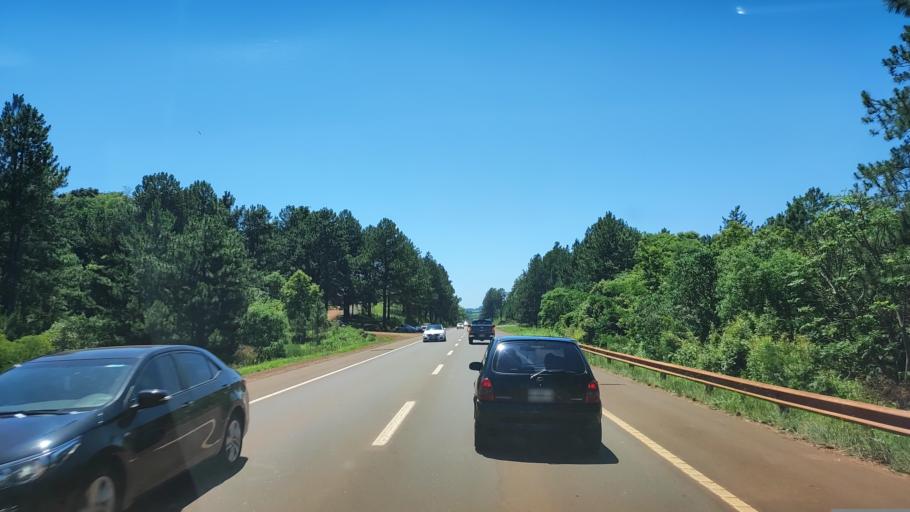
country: AR
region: Misiones
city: Aristobulo del Valle
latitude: -27.0846
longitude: -54.8058
